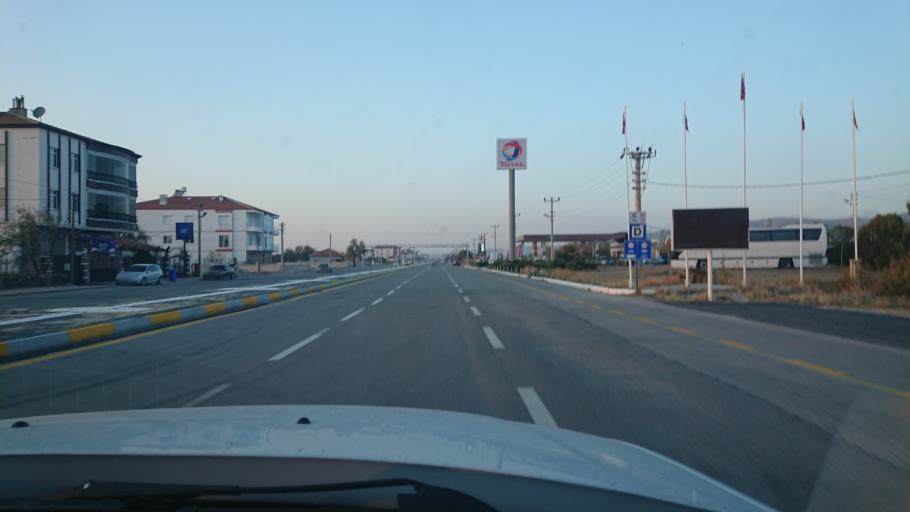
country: TR
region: Aksaray
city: Aksaray
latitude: 38.3313
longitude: 34.0505
